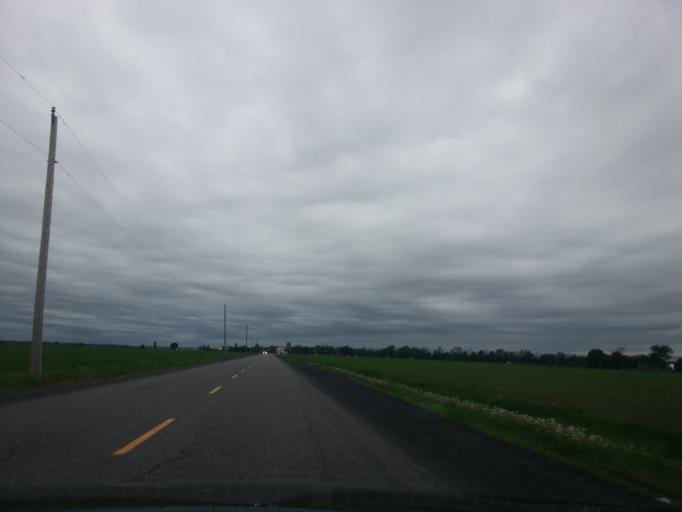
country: CA
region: Ontario
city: Bells Corners
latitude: 45.2541
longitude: -75.8398
